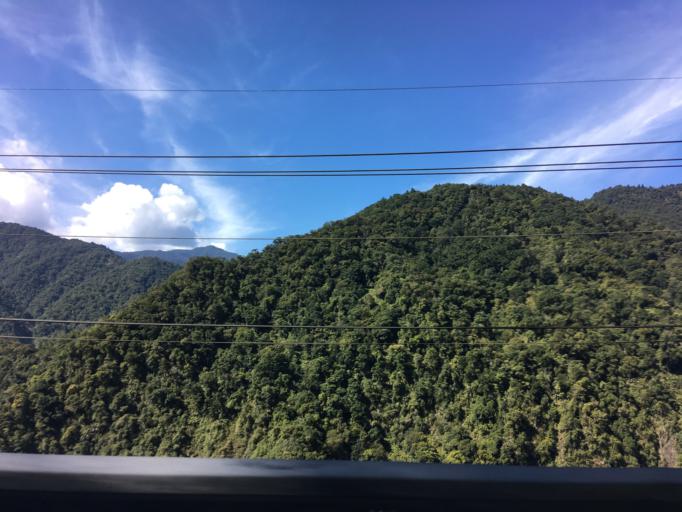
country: TW
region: Taiwan
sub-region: Yilan
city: Yilan
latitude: 24.5556
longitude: 121.5063
